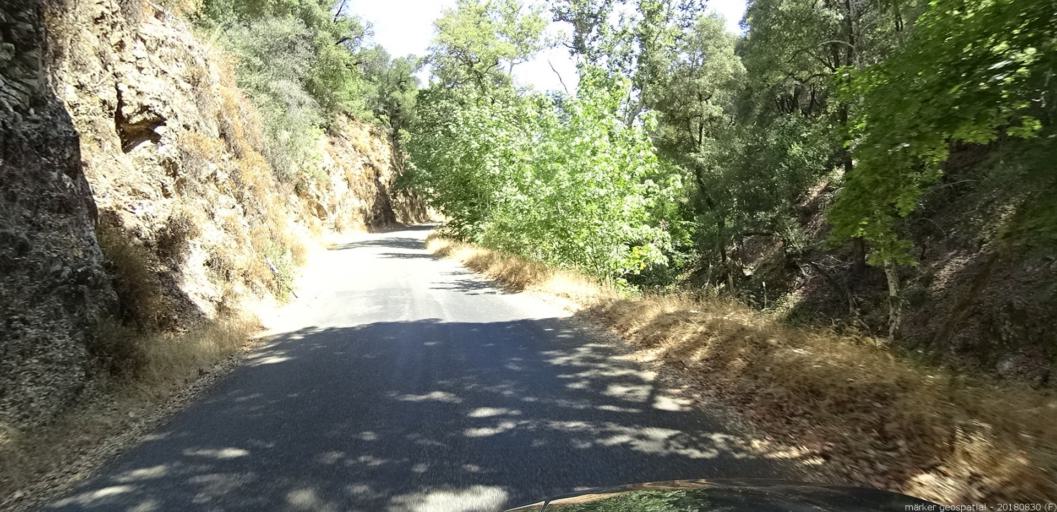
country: US
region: California
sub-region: Monterey County
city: King City
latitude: 36.0135
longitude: -121.4146
